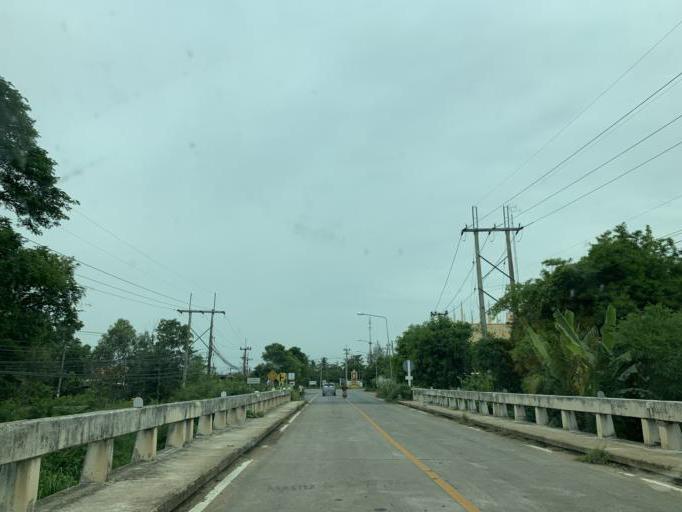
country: TH
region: Nakhon Sawan
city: Lat Yao
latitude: 15.6753
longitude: 99.8250
